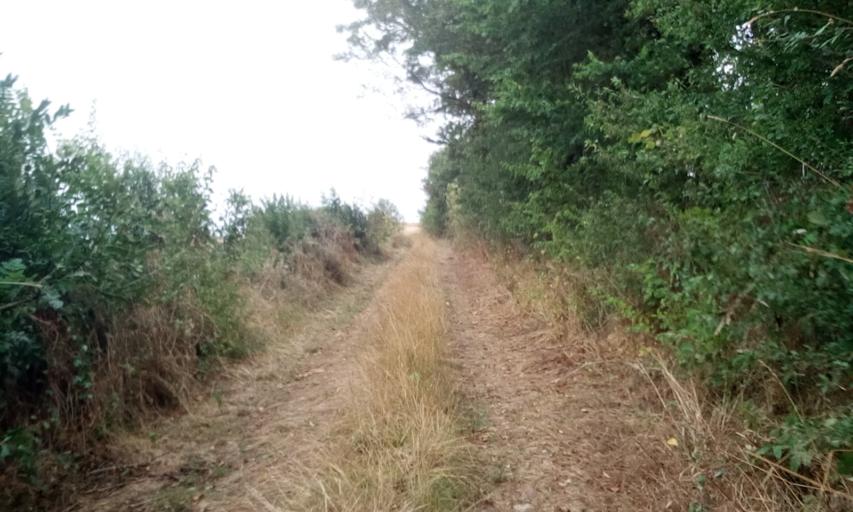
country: FR
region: Lower Normandy
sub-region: Departement du Calvados
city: Fontaine-Etoupefour
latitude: 49.1352
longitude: -0.4629
